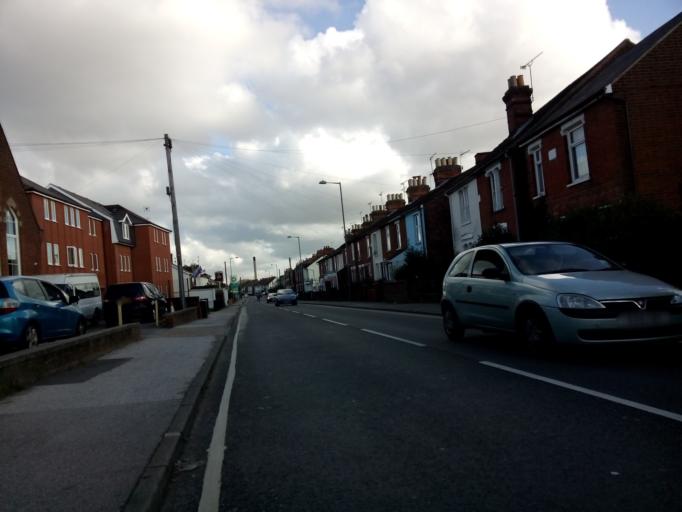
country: GB
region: England
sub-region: Suffolk
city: Ipswich
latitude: 52.0593
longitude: 1.1868
